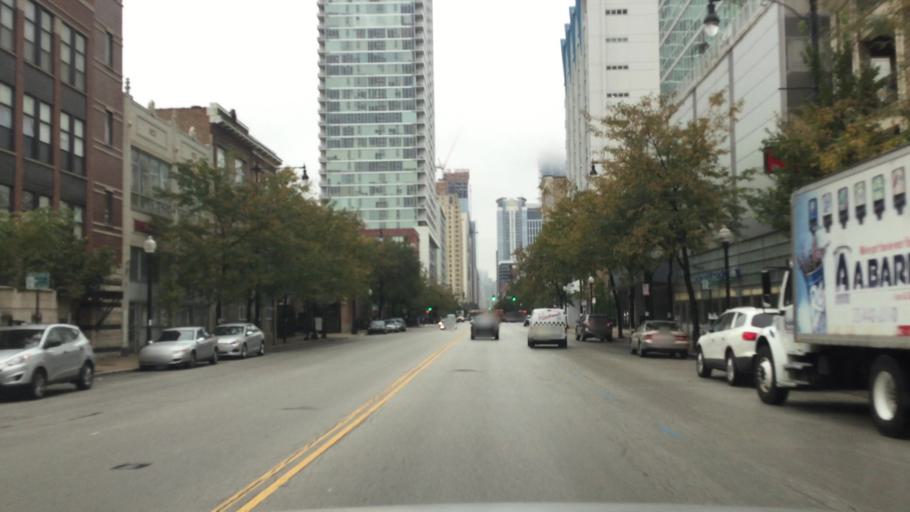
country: US
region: Illinois
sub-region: Cook County
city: Chicago
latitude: 41.8561
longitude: -87.6241
